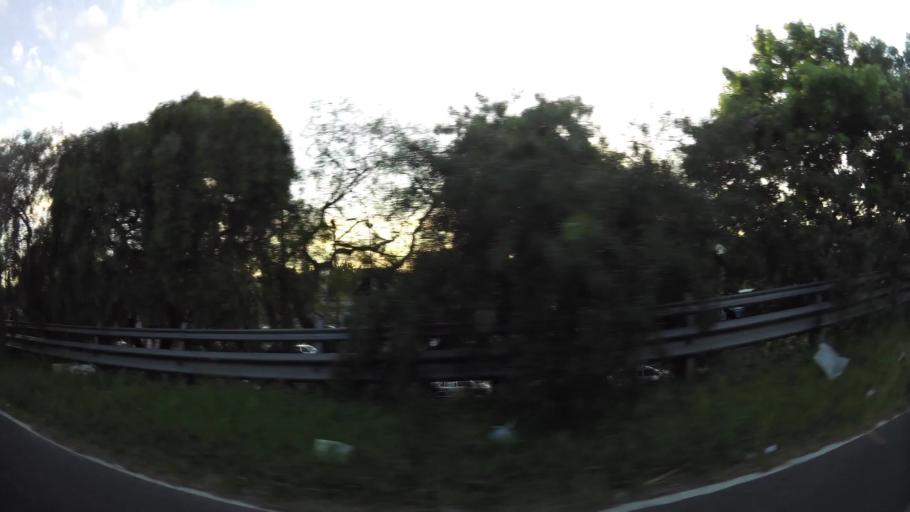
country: AR
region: Buenos Aires
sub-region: Partido de Vicente Lopez
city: Olivos
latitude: -34.5313
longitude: -58.5045
